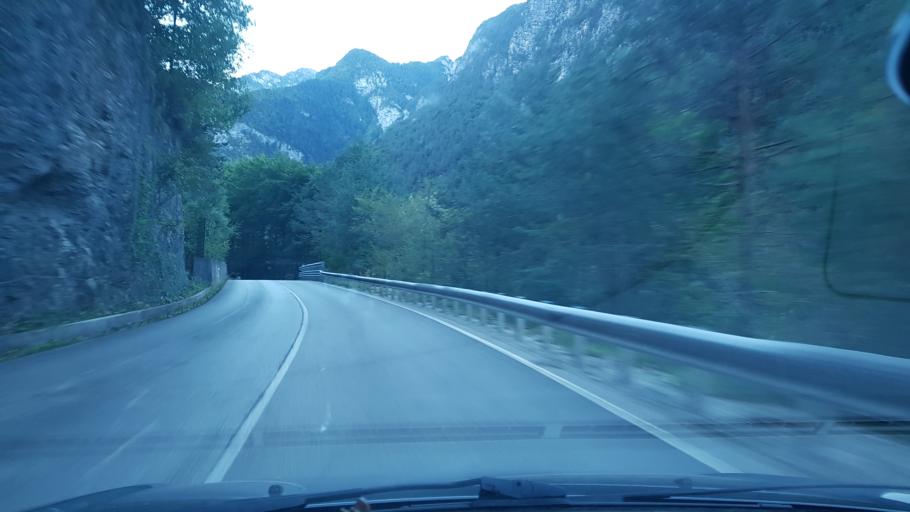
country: IT
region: Veneto
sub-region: Provincia di Belluno
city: Forno di Zoldo
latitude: 46.3187
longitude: 12.2317
